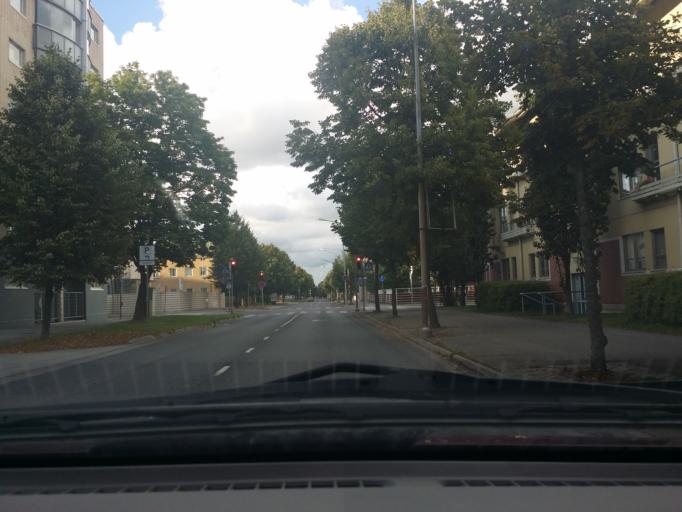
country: FI
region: Satakunta
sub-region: Pori
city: Pori
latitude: 61.4844
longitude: 21.8012
